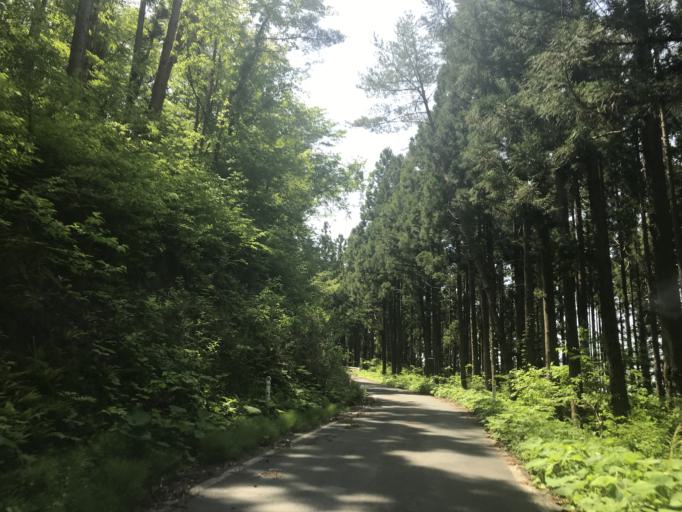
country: JP
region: Iwate
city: Ichinoseki
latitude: 38.9692
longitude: 141.2240
